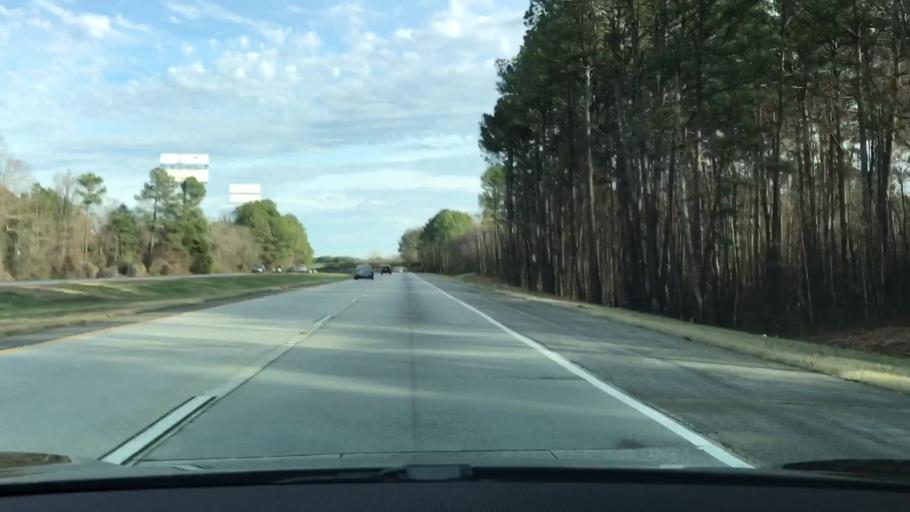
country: US
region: Georgia
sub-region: Taliaferro County
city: Crawfordville
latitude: 33.5283
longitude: -82.9620
